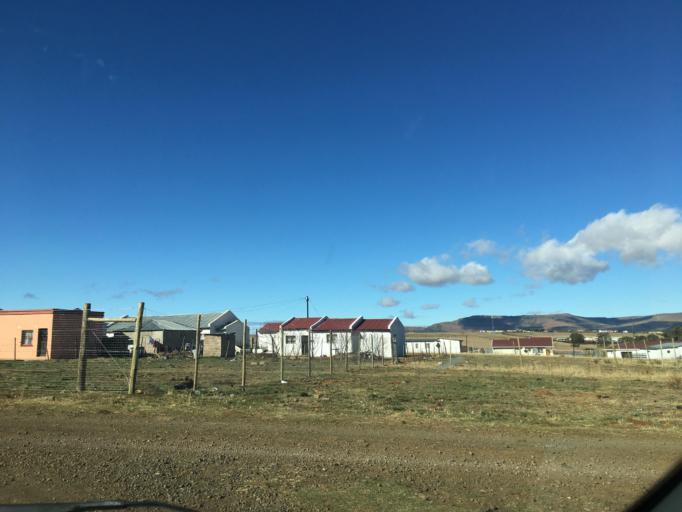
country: ZA
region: Eastern Cape
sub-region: Chris Hani District Municipality
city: Cala
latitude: -31.5373
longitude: 27.6923
